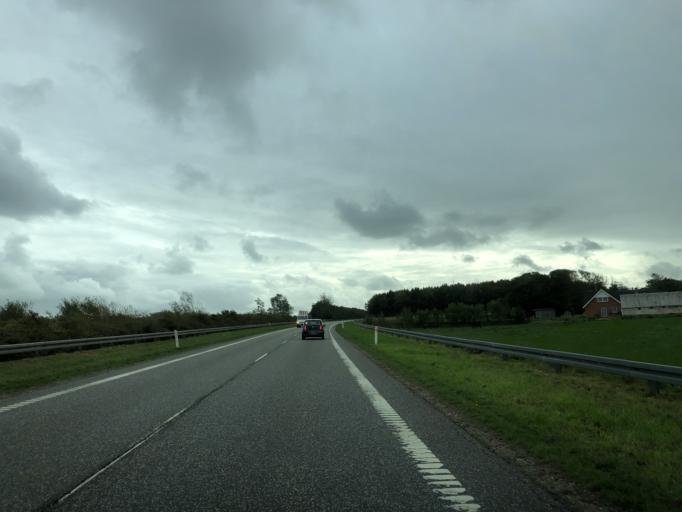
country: DK
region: North Denmark
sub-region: Thisted Kommune
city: Hurup
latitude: 56.7801
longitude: 8.4663
